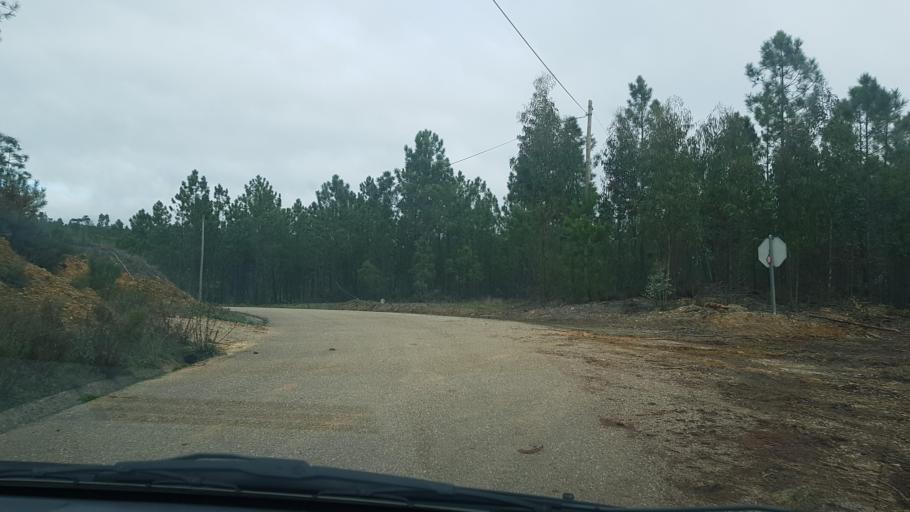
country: PT
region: Castelo Branco
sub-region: Vila de Rei
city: Vila de Rei
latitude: 39.5925
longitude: -8.1186
